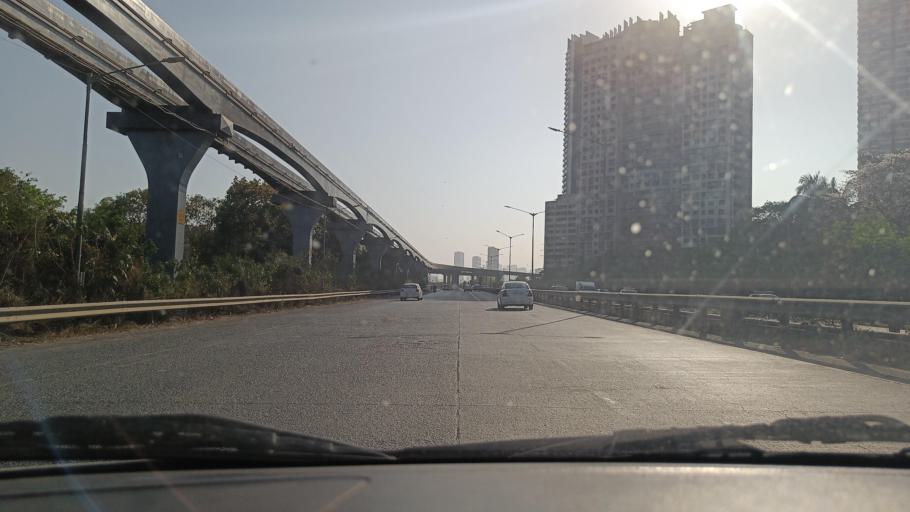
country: IN
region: Maharashtra
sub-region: Mumbai Suburban
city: Mumbai
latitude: 19.0259
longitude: 72.8817
